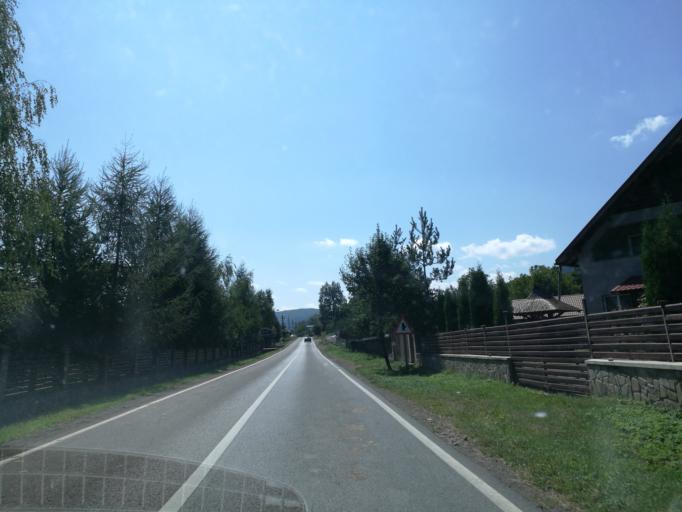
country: RO
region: Suceava
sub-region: Comuna Putna
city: Gura Putnei
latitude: 47.8925
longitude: 25.6104
